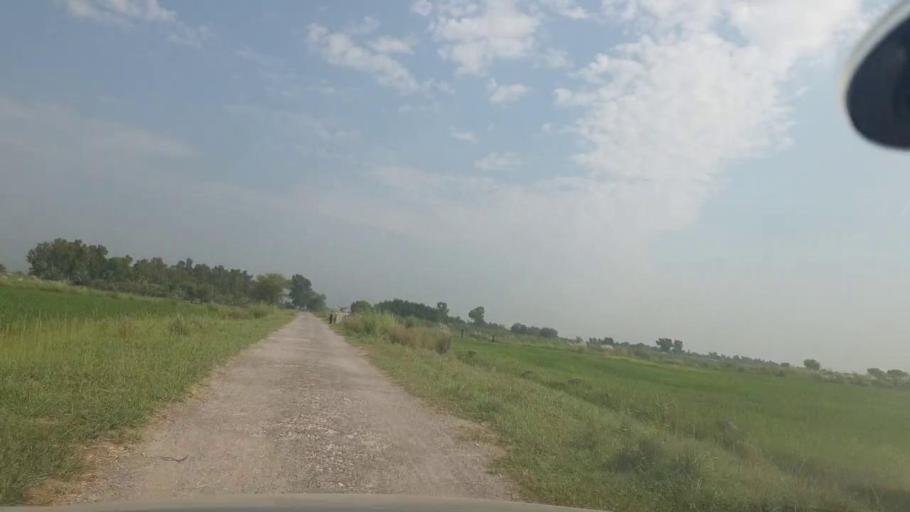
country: PK
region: Balochistan
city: Mehrabpur
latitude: 28.0502
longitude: 68.1229
